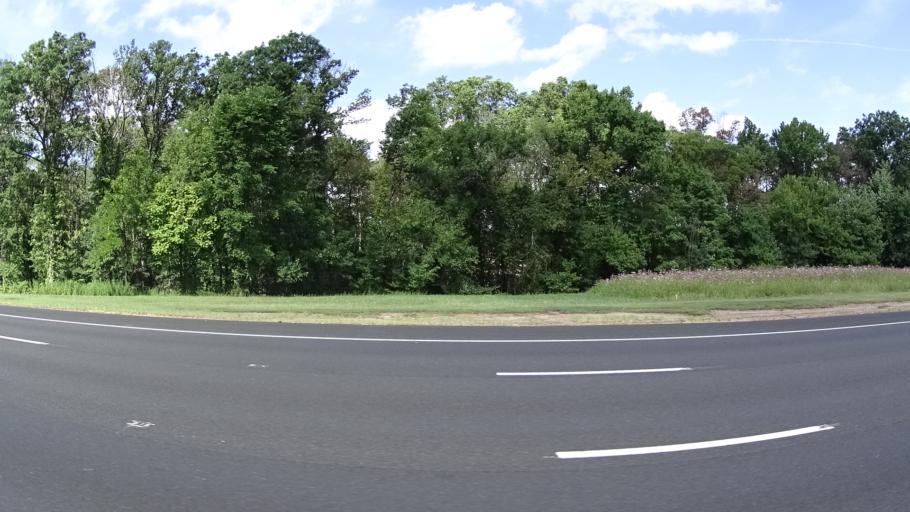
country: US
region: New Jersey
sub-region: Middlesex County
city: Iselin
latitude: 40.5890
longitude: -74.3261
